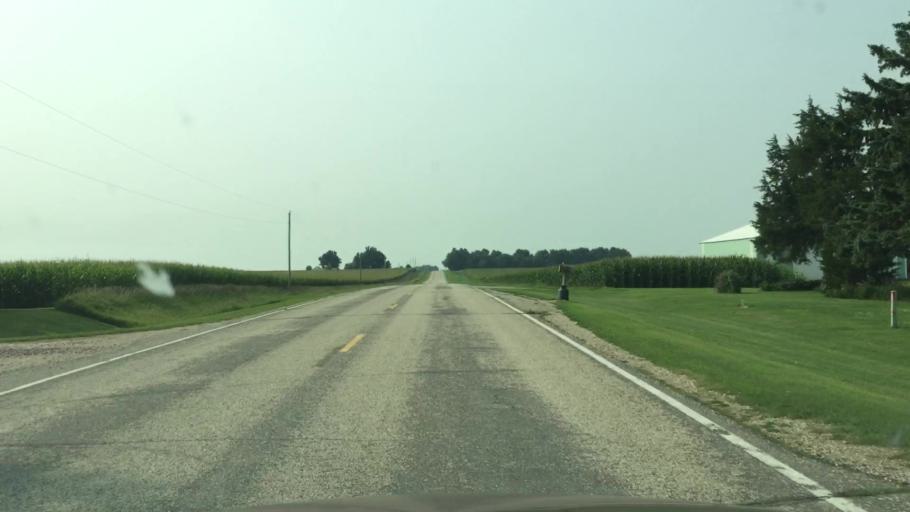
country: US
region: Iowa
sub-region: O'Brien County
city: Sheldon
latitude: 43.2698
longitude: -95.7829
